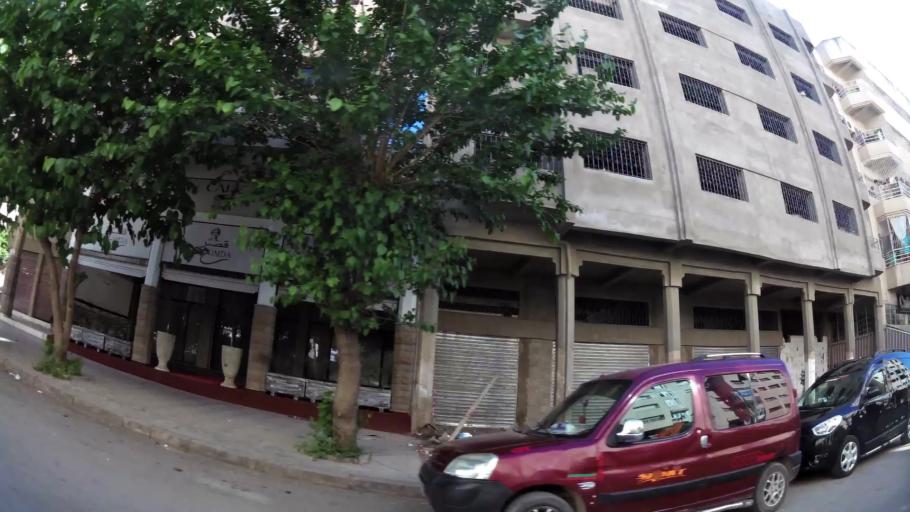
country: MA
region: Fes-Boulemane
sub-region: Fes
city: Fes
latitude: 34.0121
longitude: -4.9674
